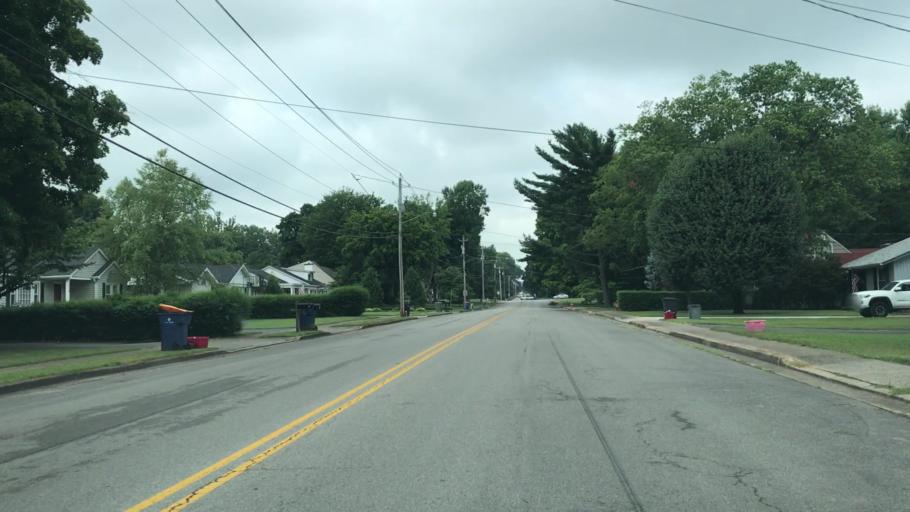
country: US
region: Kentucky
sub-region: Warren County
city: Bowling Green
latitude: 36.9833
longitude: -86.4248
